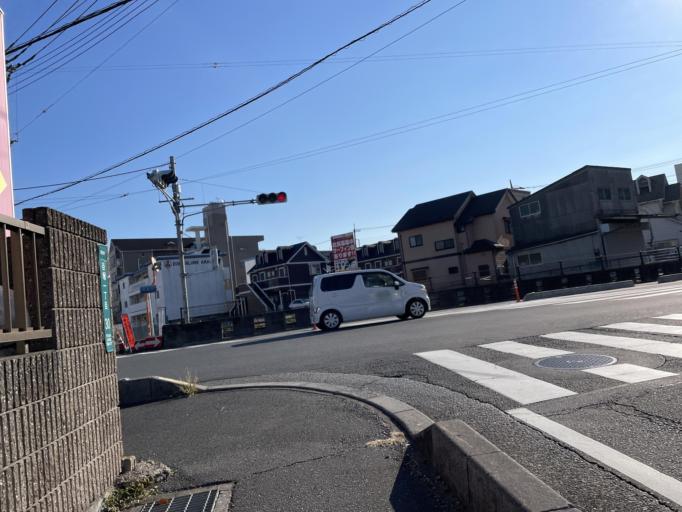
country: JP
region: Saitama
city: Soka
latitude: 35.8084
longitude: 139.8015
